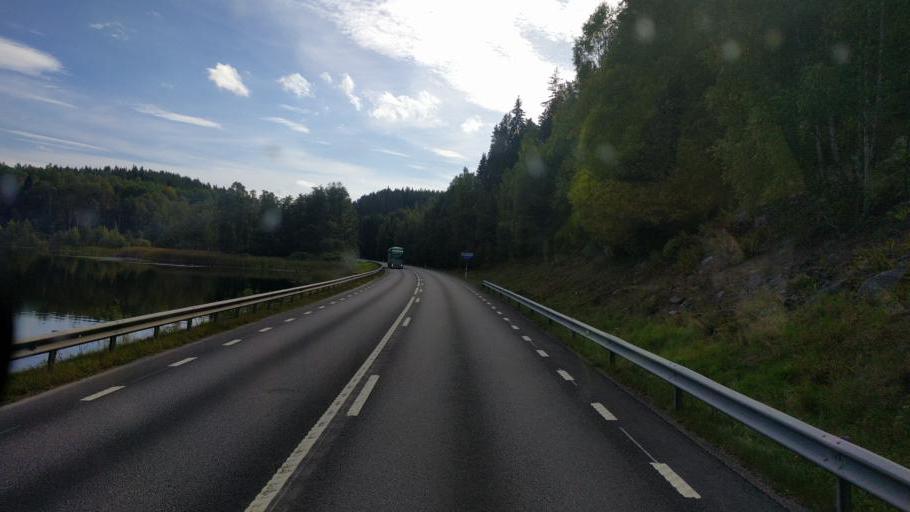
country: SE
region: OEstergoetland
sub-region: Kinda Kommun
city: Kisa
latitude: 57.9570
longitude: 15.6601
